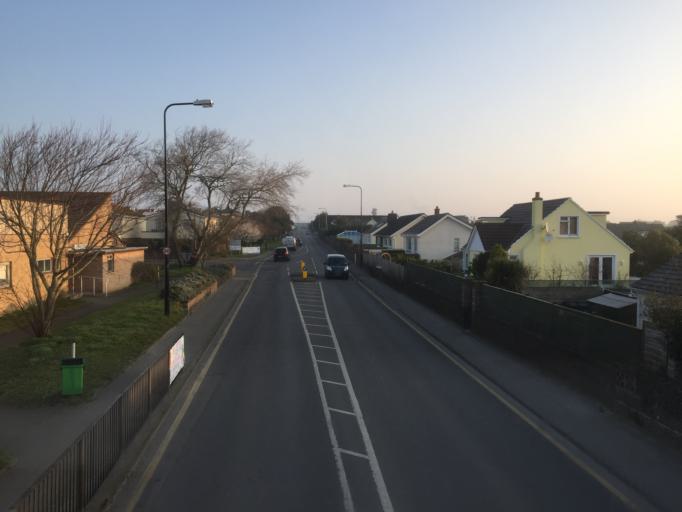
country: JE
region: St Helier
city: Saint Helier
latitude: 49.1945
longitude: -2.1988
